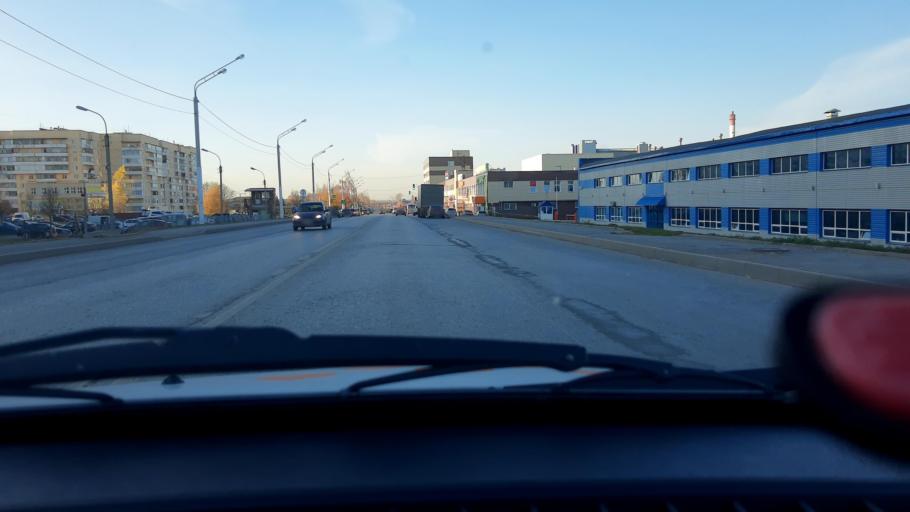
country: RU
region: Bashkortostan
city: Iglino
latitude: 54.7570
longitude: 56.2480
